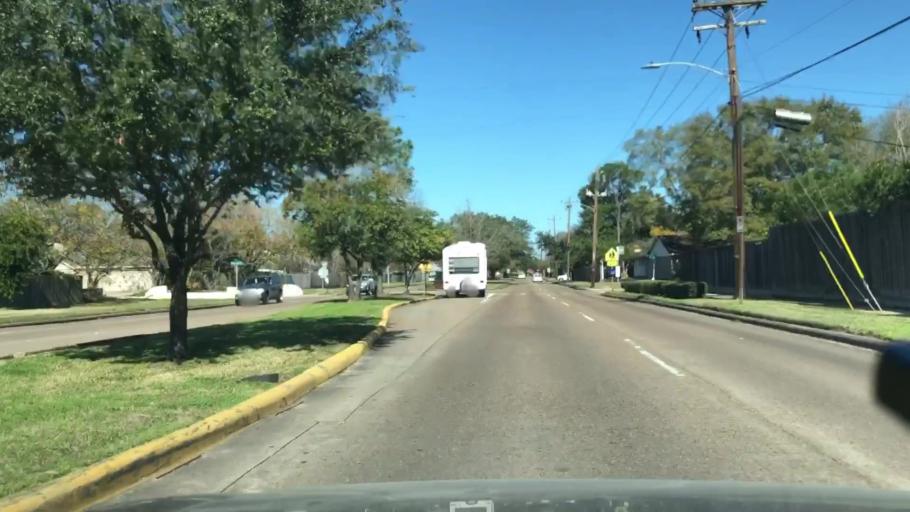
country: US
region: Texas
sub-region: Harris County
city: Bellaire
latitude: 29.6812
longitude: -95.4927
